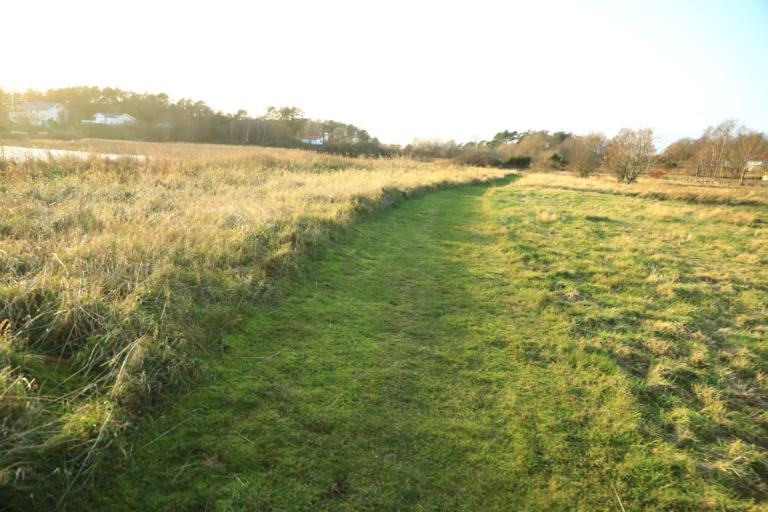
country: SE
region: Halland
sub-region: Varbergs Kommun
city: Varberg
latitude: 57.1911
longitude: 12.2020
